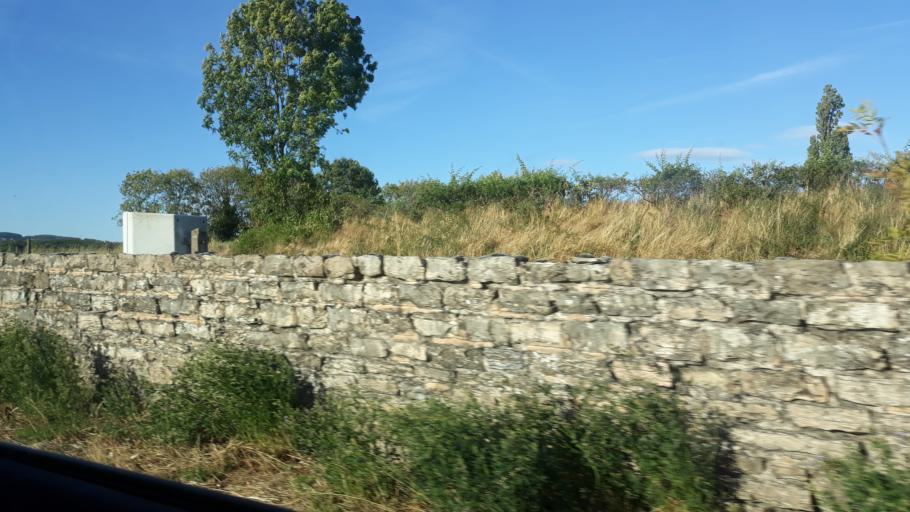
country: FR
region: Bourgogne
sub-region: Departement de Saone-et-Loire
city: Torcy
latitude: 46.7734
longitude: 4.4481
